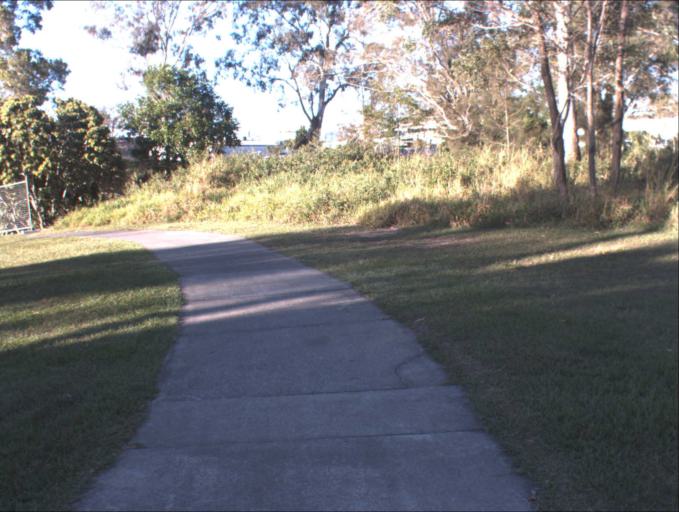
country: AU
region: Queensland
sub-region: Logan
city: Logan City
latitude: -27.6346
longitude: 153.1290
